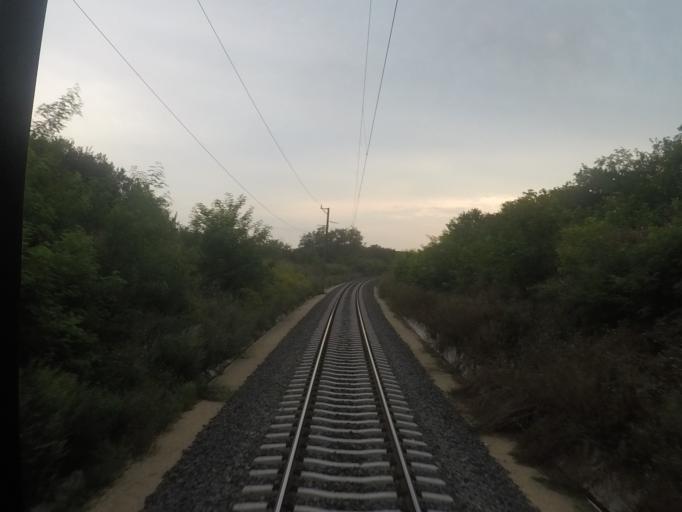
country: HU
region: Fejer
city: Lepseny
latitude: 46.9762
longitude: 18.2328
